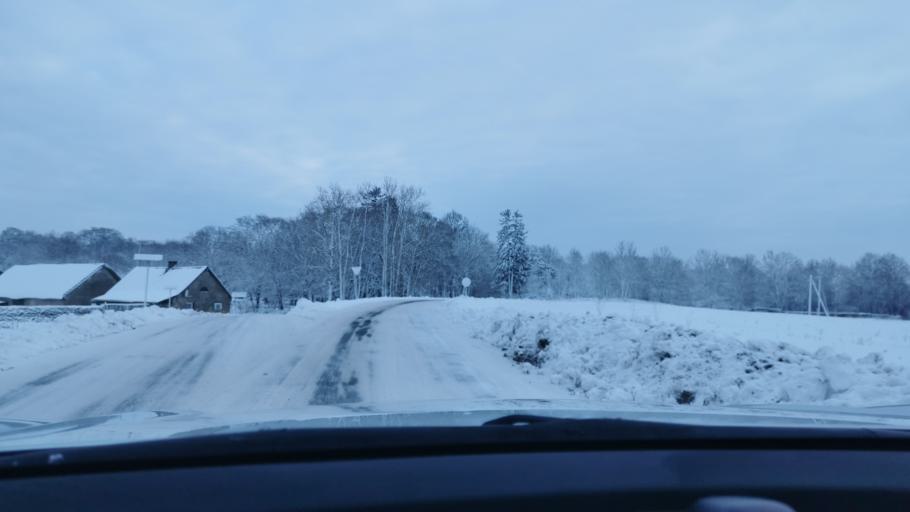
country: EE
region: Laeaene-Virumaa
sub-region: Viru-Nigula vald
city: Kunda
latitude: 59.4829
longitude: 26.5209
